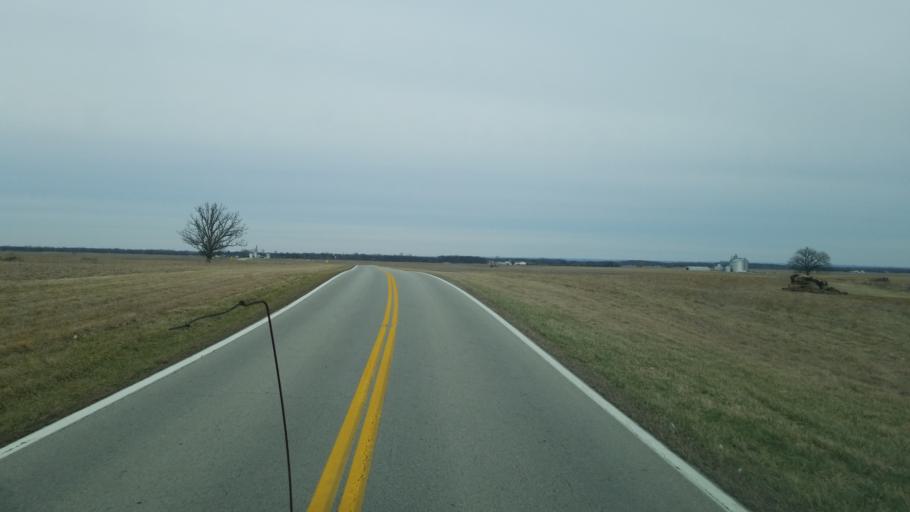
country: US
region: Ohio
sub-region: Ross County
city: Frankfort
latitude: 39.4866
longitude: -83.1768
